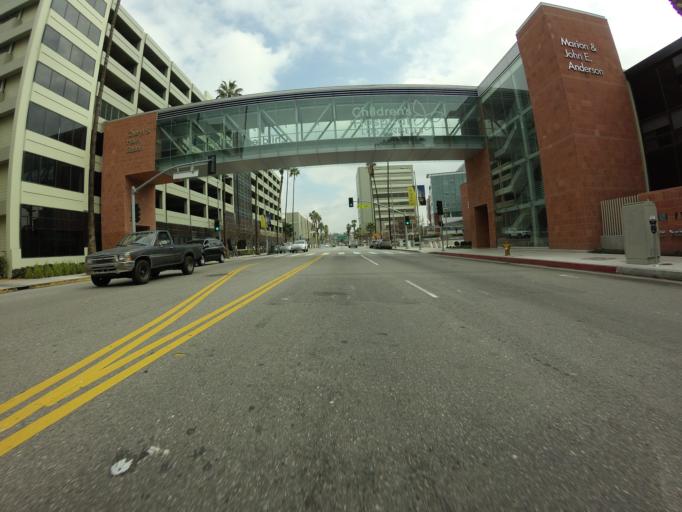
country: US
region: California
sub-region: Los Angeles County
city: Silver Lake
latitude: 34.0982
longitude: -118.2908
